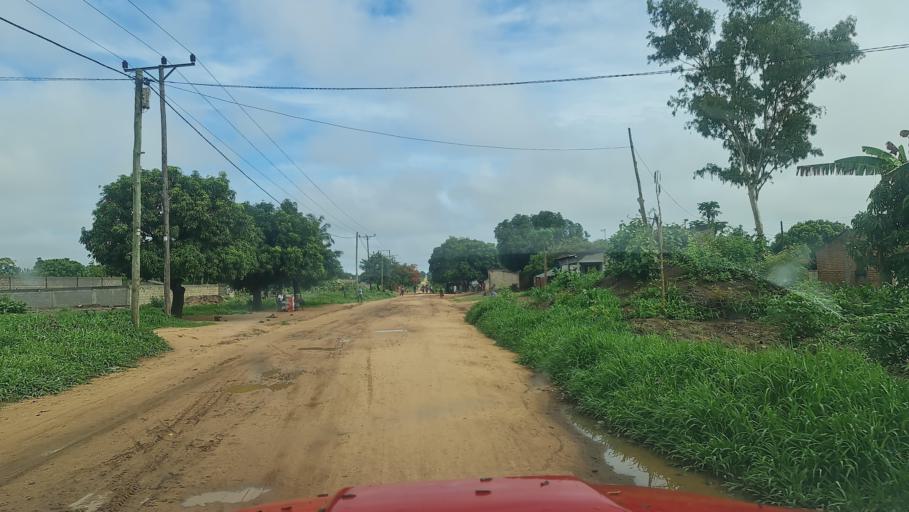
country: MW
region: Southern Region
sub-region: Nsanje District
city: Nsanje
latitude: -17.3189
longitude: 35.5920
